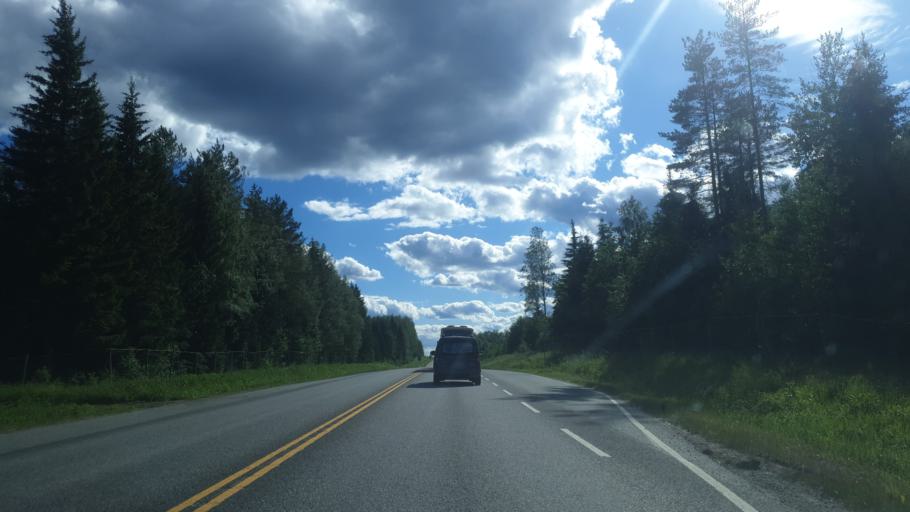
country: FI
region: Southern Savonia
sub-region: Pieksaemaeki
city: Juva
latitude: 61.8318
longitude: 27.6462
